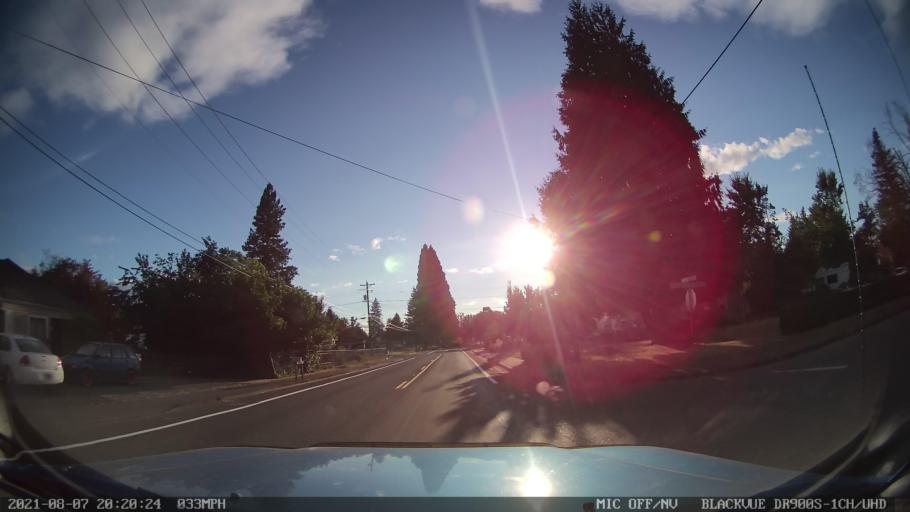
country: US
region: Oregon
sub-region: Marion County
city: Four Corners
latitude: 44.9540
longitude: -123.0020
